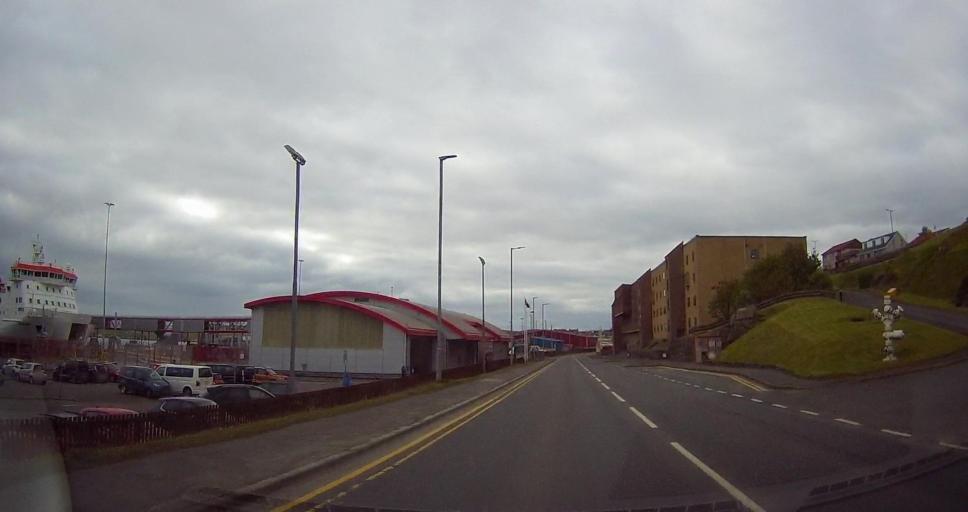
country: GB
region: Scotland
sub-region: Shetland Islands
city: Lerwick
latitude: 60.1633
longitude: -1.1599
